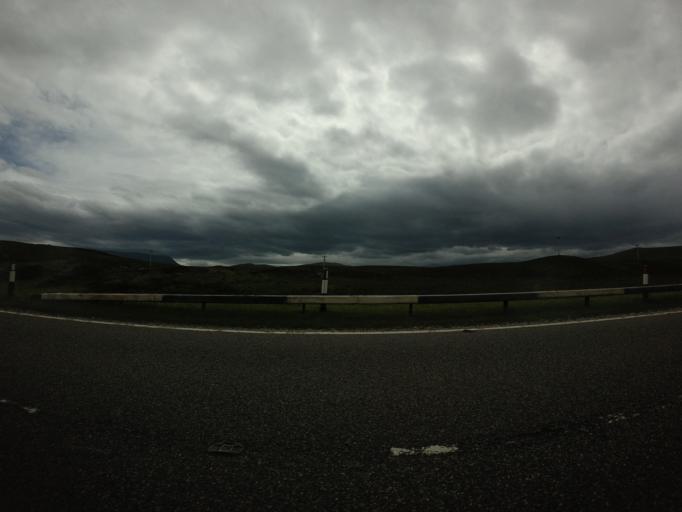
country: GB
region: Scotland
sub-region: Highland
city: Dingwall
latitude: 57.6932
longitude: -4.7402
